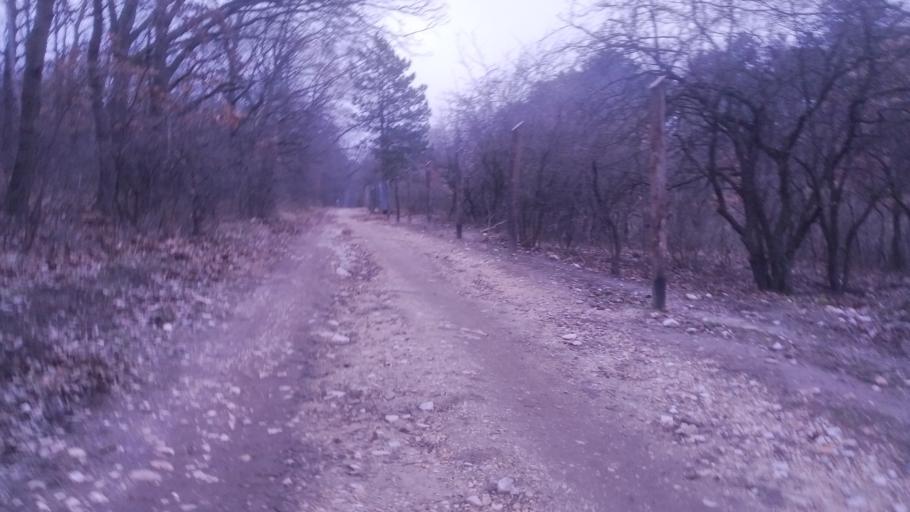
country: HU
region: Komarom-Esztergom
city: Dunaalmas
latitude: 47.7040
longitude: 18.3209
